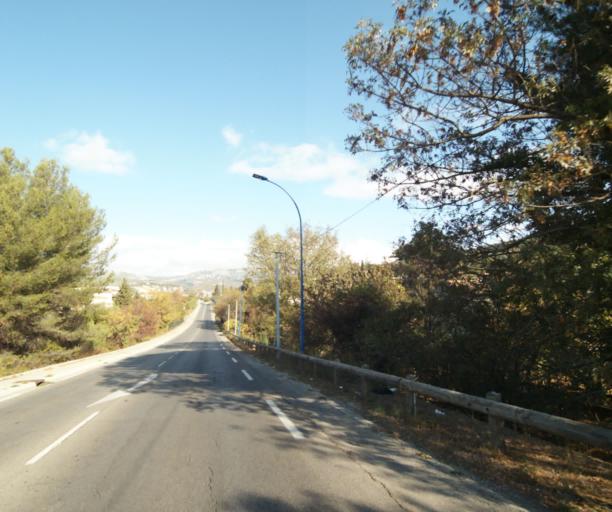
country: FR
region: Provence-Alpes-Cote d'Azur
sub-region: Departement des Bouches-du-Rhone
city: Allauch
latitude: 43.3462
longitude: 5.4872
